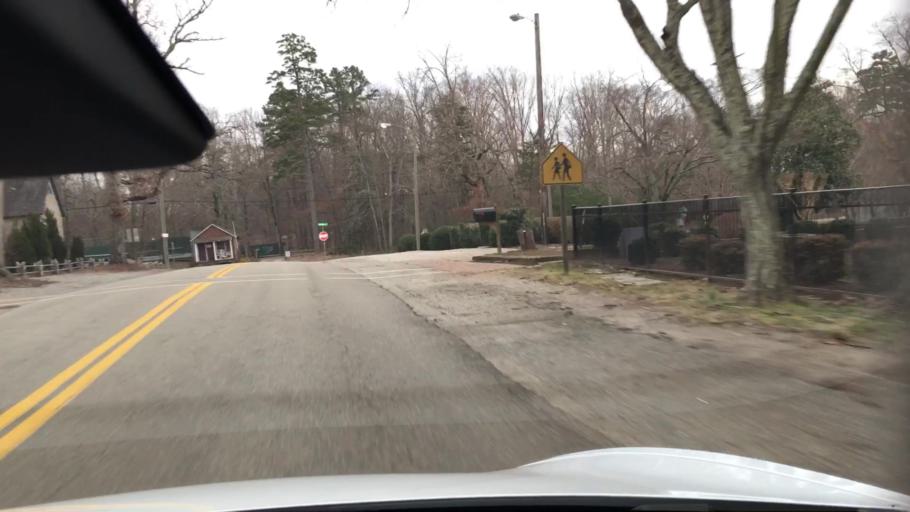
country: US
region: Virginia
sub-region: Chesterfield County
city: Bon Air
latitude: 37.5253
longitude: -77.5596
